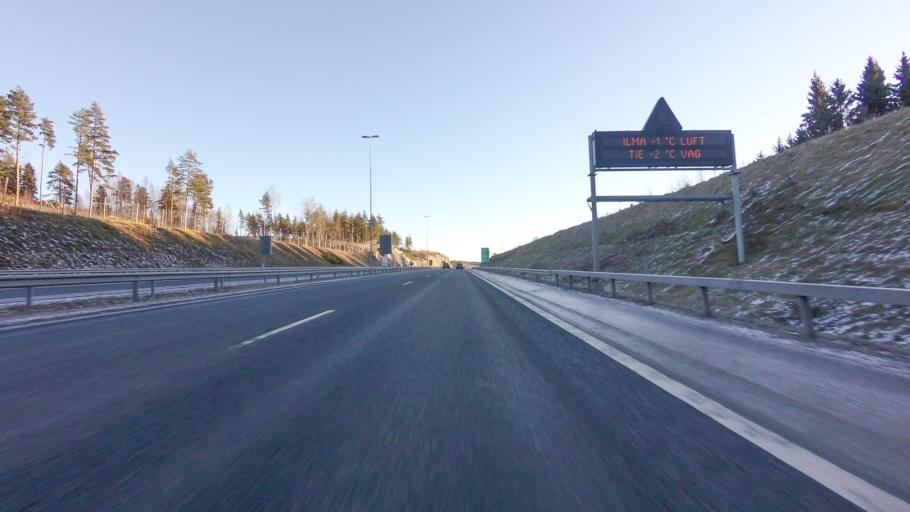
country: FI
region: Uusimaa
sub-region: Helsinki
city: Lohja
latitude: 60.2890
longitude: 24.0793
